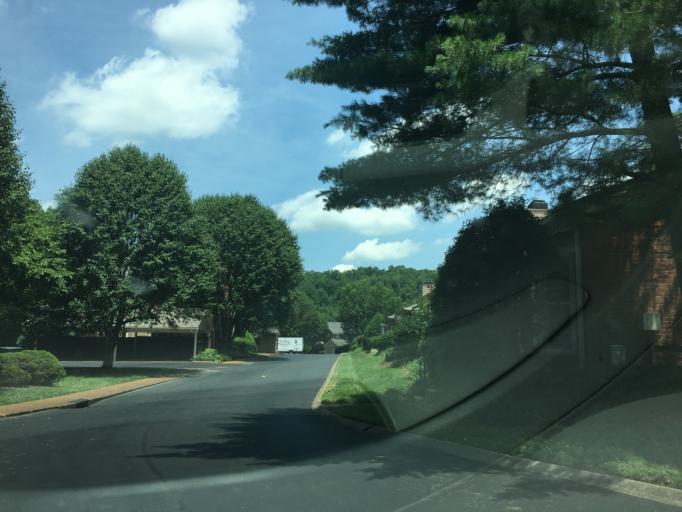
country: US
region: Tennessee
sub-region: Davidson County
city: Belle Meade
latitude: 36.0750
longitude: -86.9101
